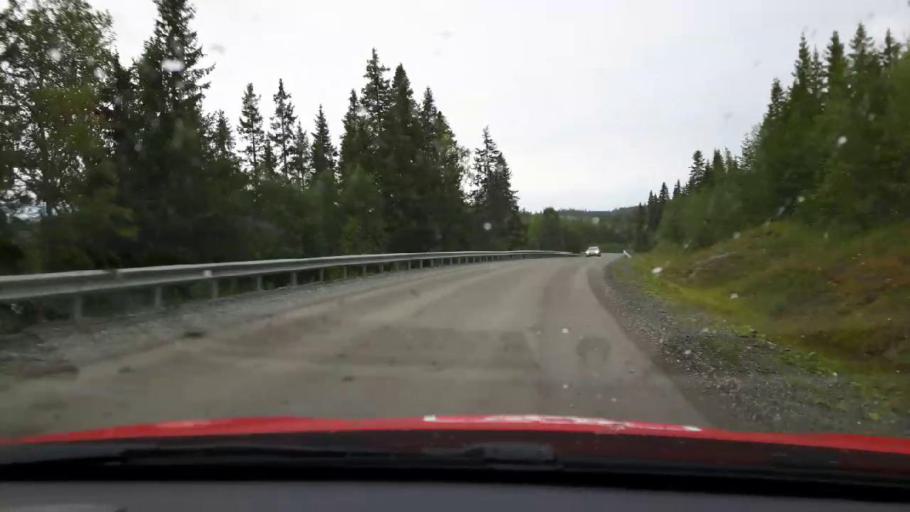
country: SE
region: Jaemtland
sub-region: Are Kommun
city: Are
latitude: 63.4418
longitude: 12.6985
